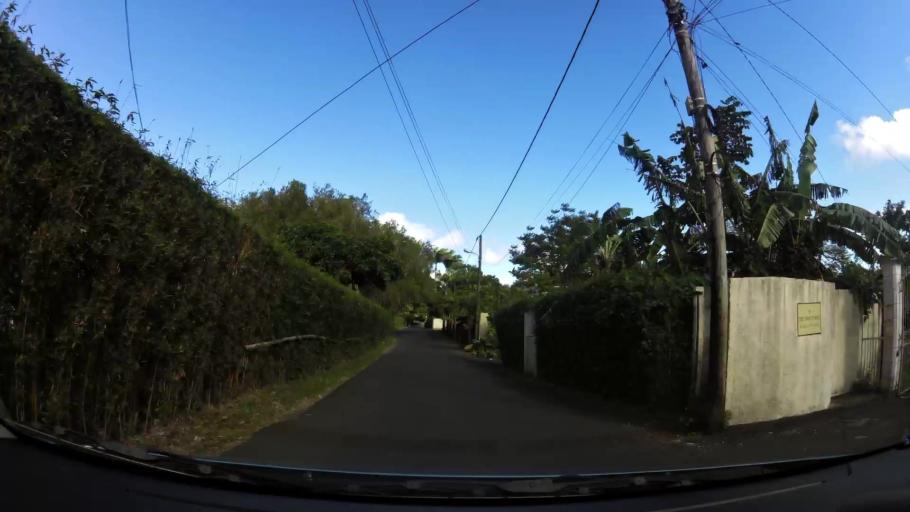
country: MU
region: Plaines Wilhems
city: Curepipe
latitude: -20.3077
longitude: 57.5045
